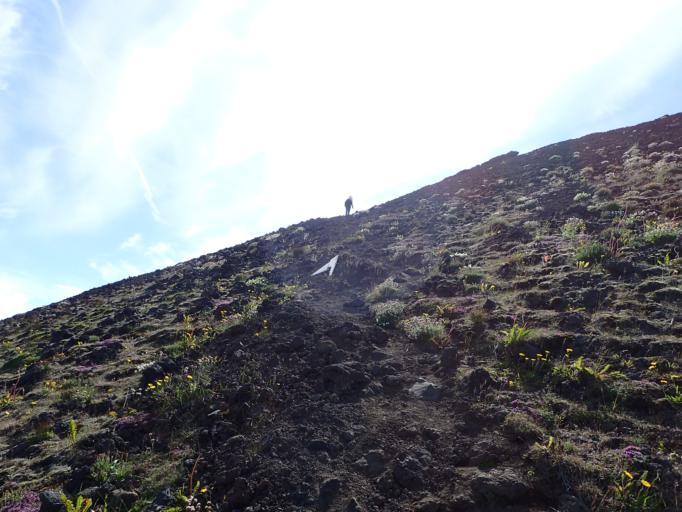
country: IS
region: South
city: Vestmannaeyjar
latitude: 63.4304
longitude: -20.2606
